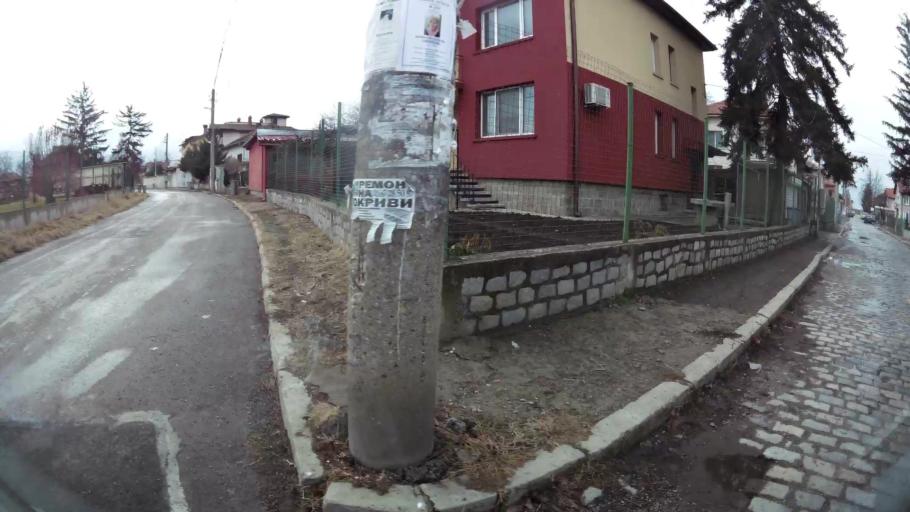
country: BG
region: Sofiya
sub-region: Obshtina Bozhurishte
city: Bozhurishte
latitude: 42.7436
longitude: 23.2647
